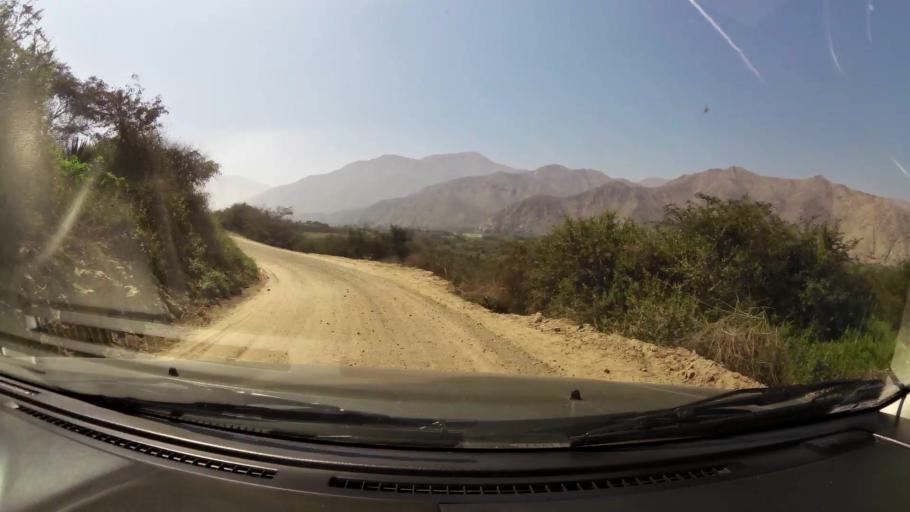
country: PE
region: Ica
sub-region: Provincia de Ica
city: Guadalupe
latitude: -13.8933
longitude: -75.6574
